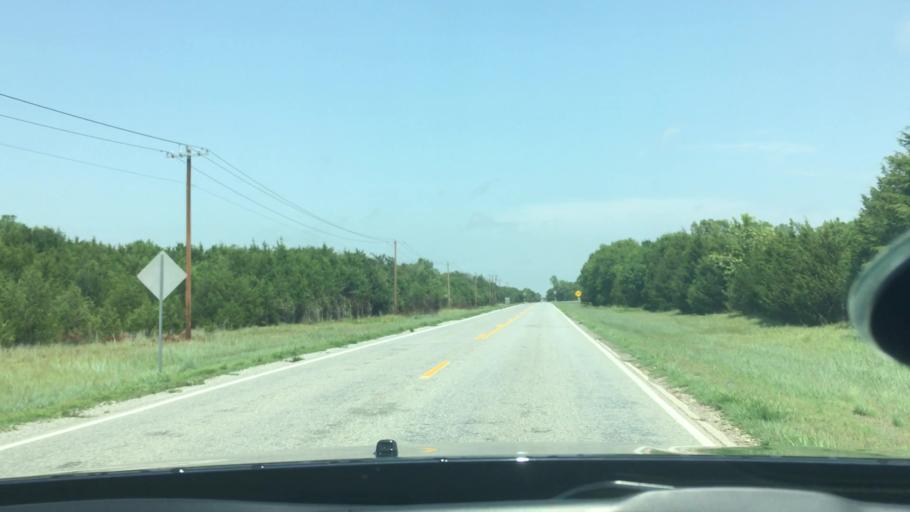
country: US
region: Oklahoma
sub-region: Murray County
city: Sulphur
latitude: 34.4126
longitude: -96.8271
